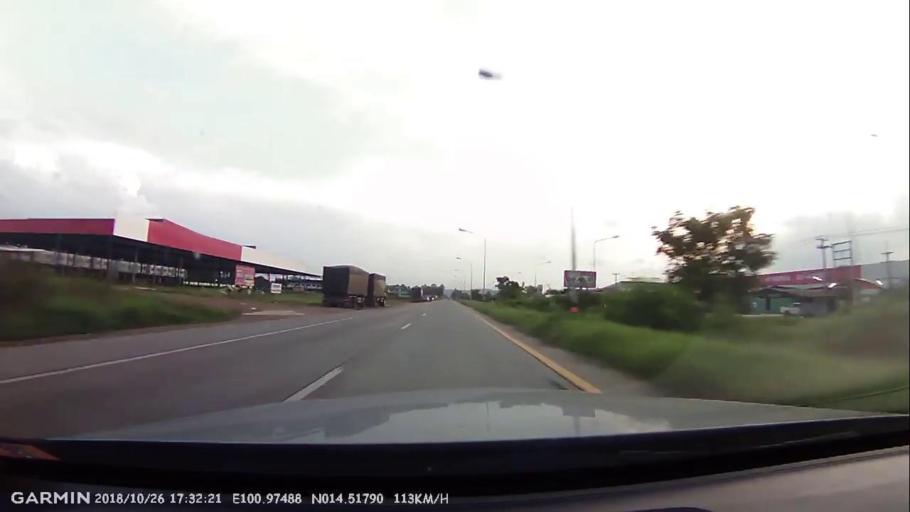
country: TH
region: Sara Buri
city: Saraburi
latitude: 14.5177
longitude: 100.9748
